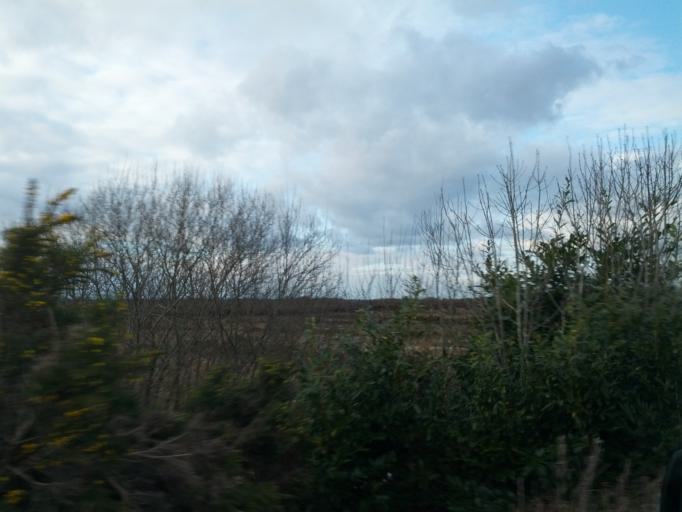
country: IE
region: Connaught
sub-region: County Galway
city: Athenry
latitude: 53.3623
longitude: -8.6667
